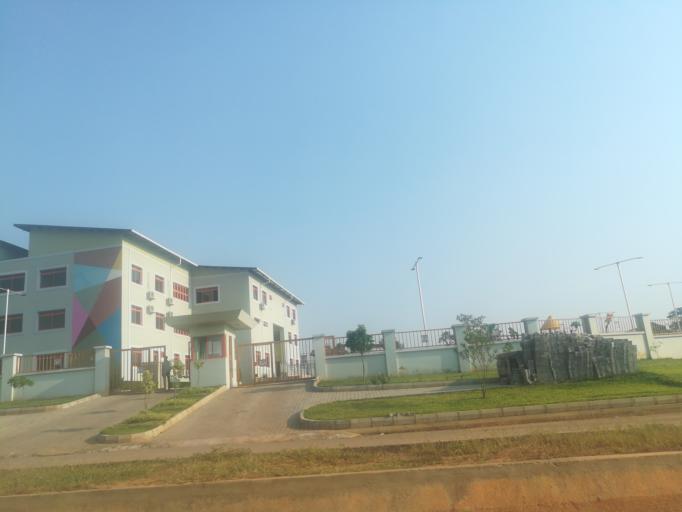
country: NG
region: Abuja Federal Capital Territory
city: Abuja
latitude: 9.0438
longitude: 7.4323
